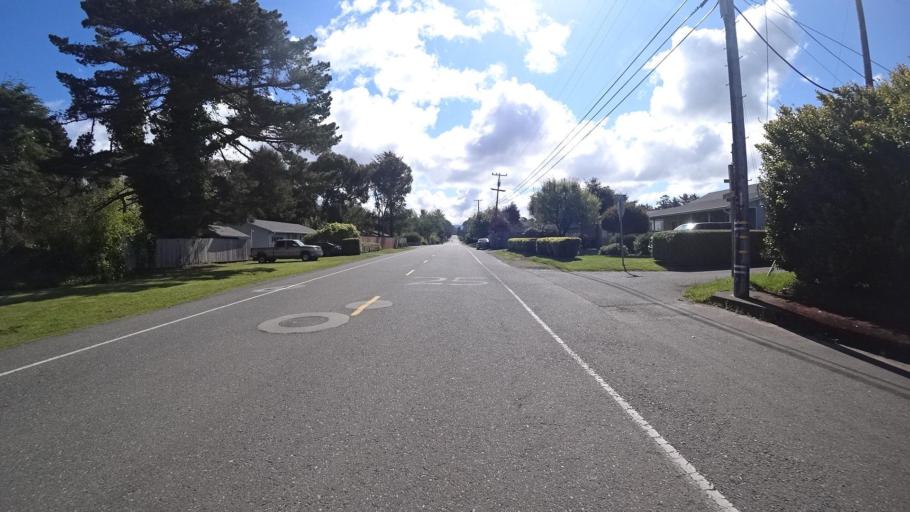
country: US
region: California
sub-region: Humboldt County
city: McKinleyville
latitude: 40.9417
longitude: -124.1235
